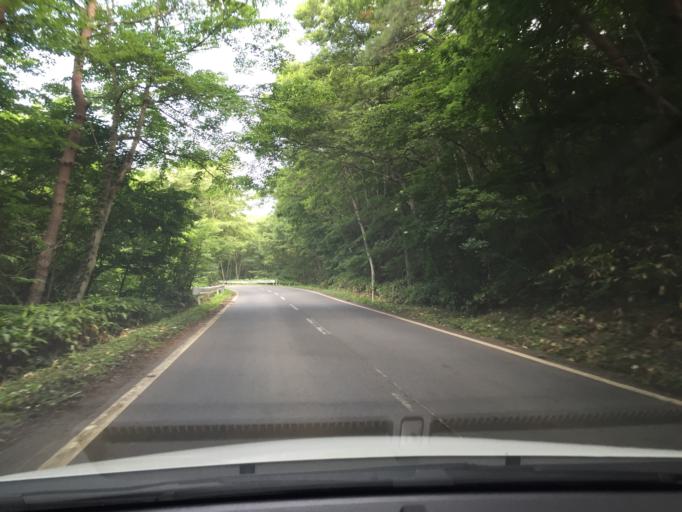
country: JP
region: Tochigi
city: Kuroiso
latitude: 37.2354
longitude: 140.0718
